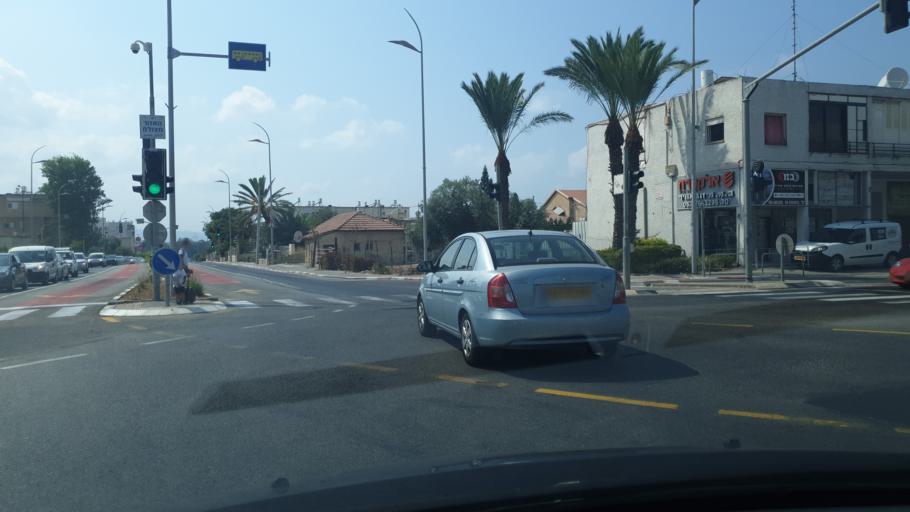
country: IL
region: Haifa
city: Qiryat Ata
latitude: 32.8125
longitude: 35.1050
